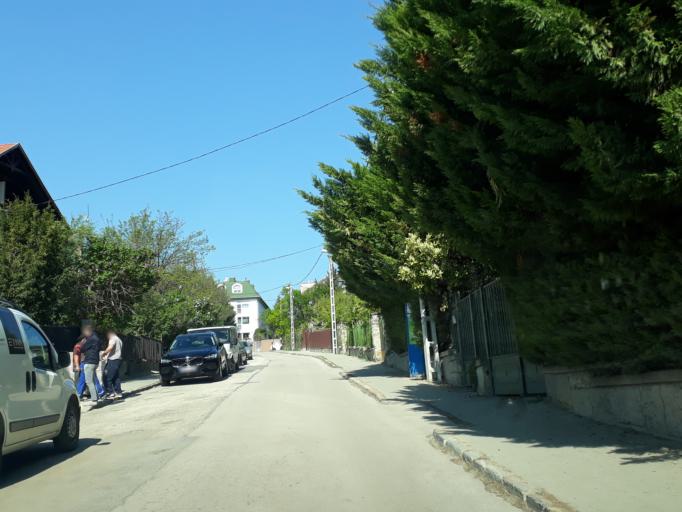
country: HU
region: Budapest
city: Budapest XII. keruelet
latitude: 47.4889
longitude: 19.0153
